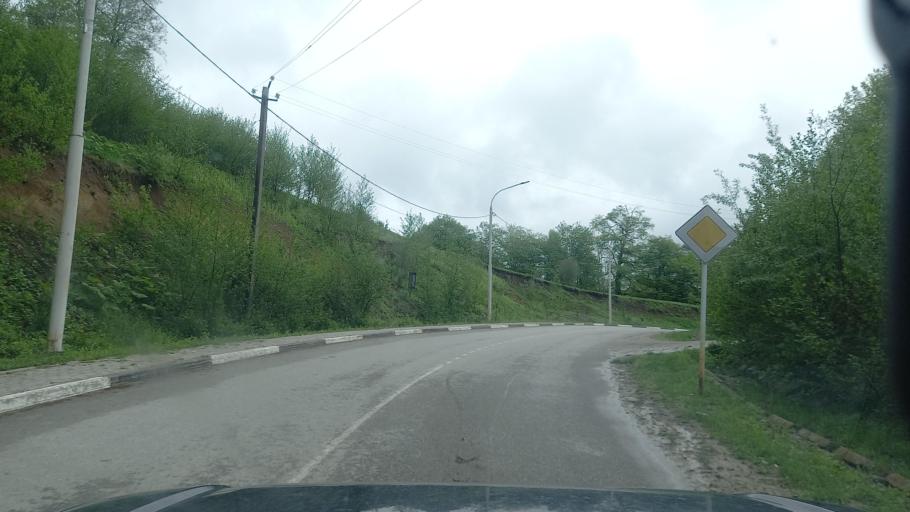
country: RU
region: Kabardino-Balkariya
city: Babugent
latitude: 43.2283
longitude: 43.5567
